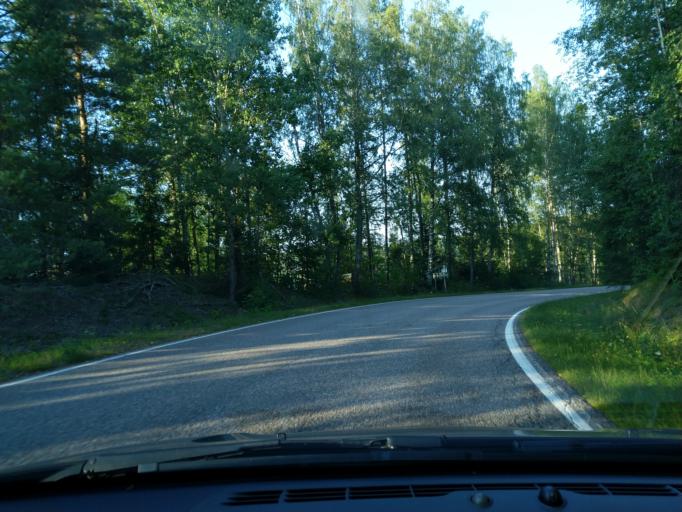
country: FI
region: Uusimaa
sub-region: Helsinki
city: Vihti
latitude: 60.5256
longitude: 24.3461
